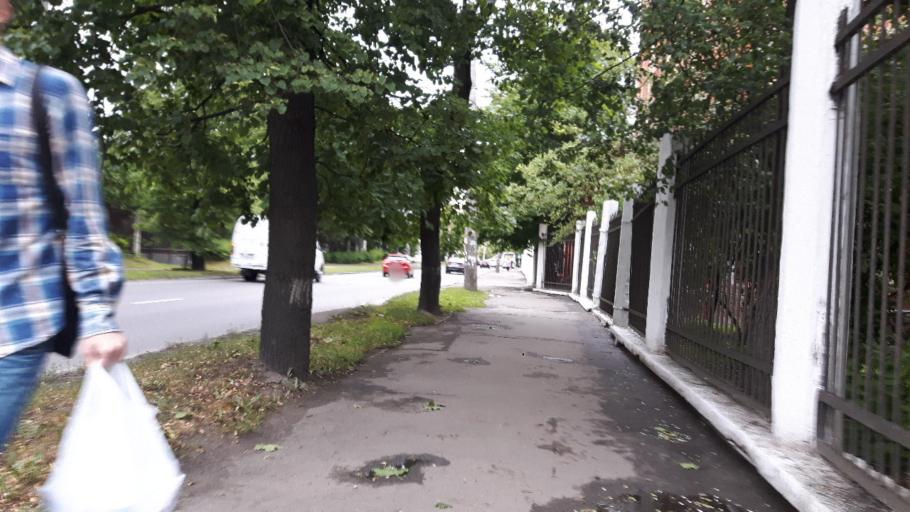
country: RU
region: Kaliningrad
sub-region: Gorod Kaliningrad
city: Kaliningrad
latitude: 54.7387
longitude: 20.4790
